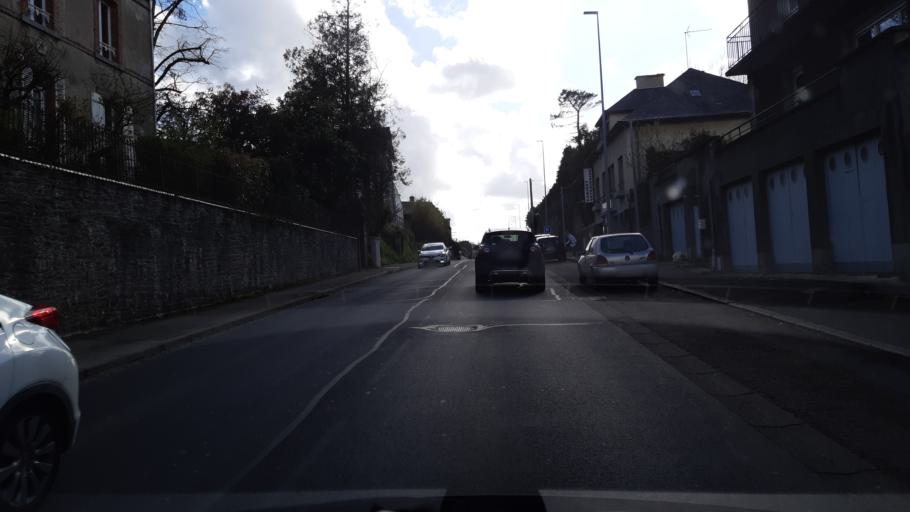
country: FR
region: Lower Normandy
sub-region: Departement de la Manche
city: Agneaux
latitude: 49.1111
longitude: -1.1028
